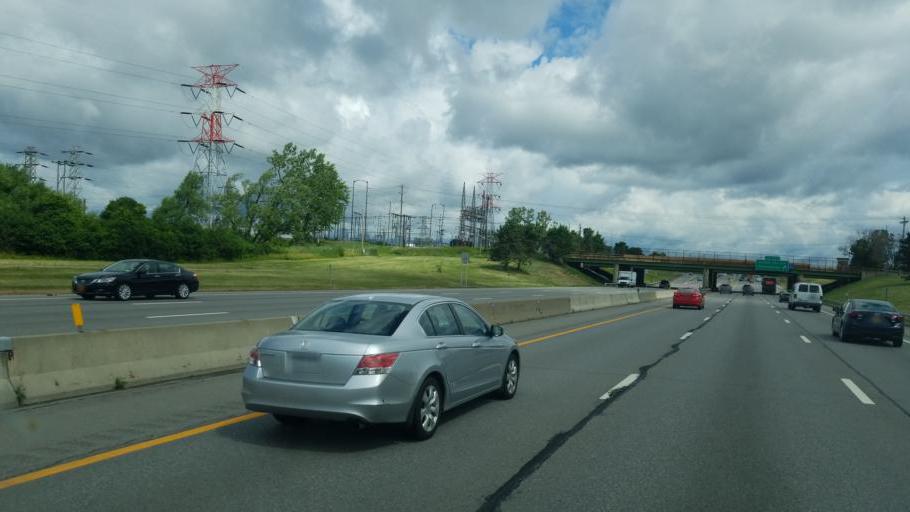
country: US
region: New York
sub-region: Erie County
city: Cheektowaga
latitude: 42.9009
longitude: -78.7669
